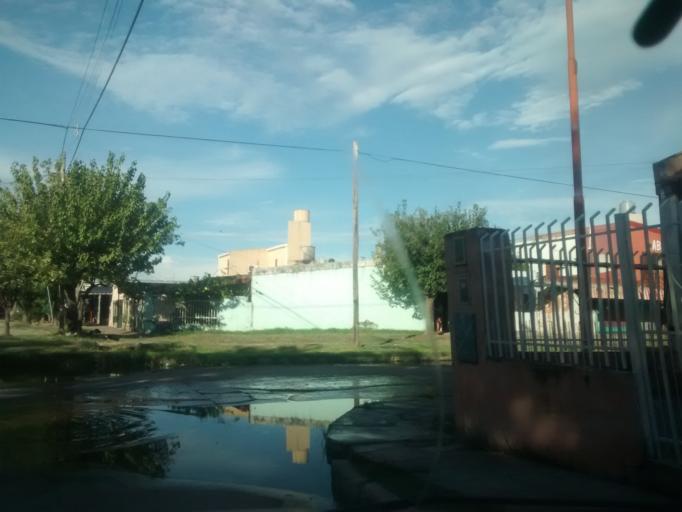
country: AR
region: Chaco
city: Resistencia
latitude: -27.4486
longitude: -59.0132
